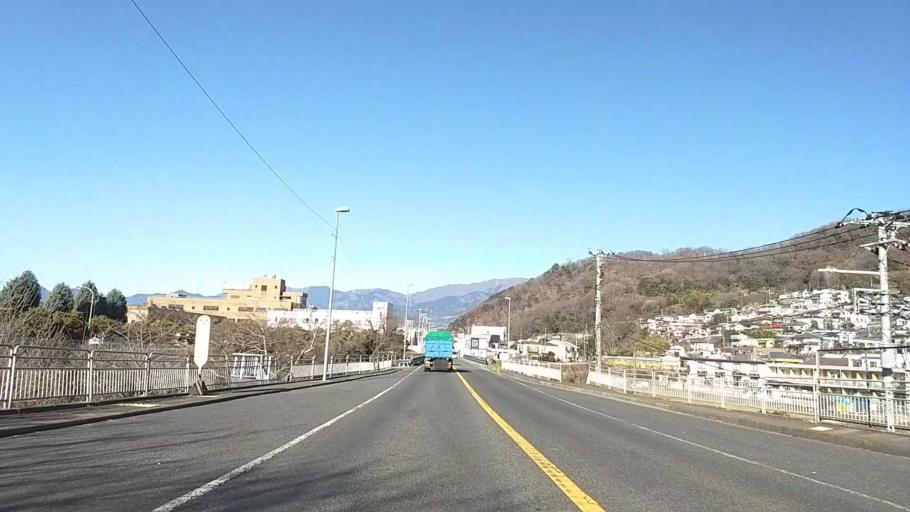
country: JP
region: Kanagawa
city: Hadano
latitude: 35.3637
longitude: 139.2457
